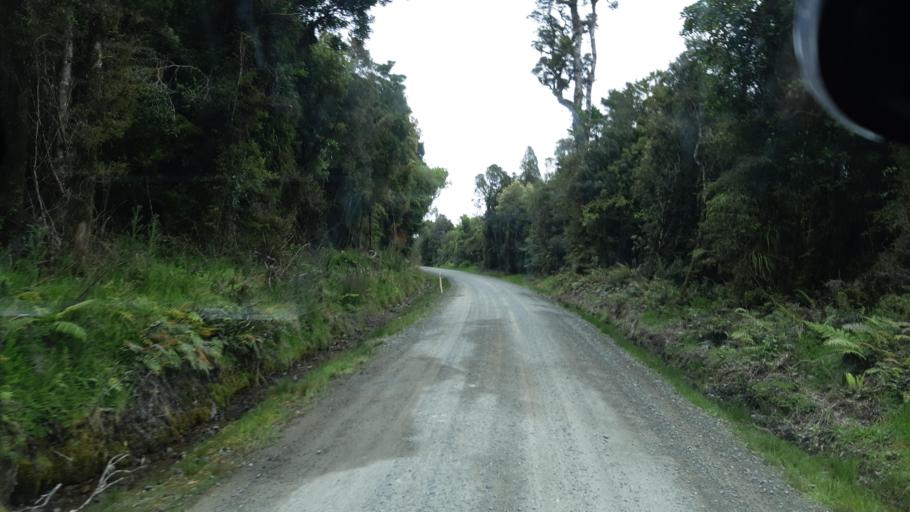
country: NZ
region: West Coast
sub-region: Grey District
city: Greymouth
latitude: -42.6415
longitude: 171.3739
